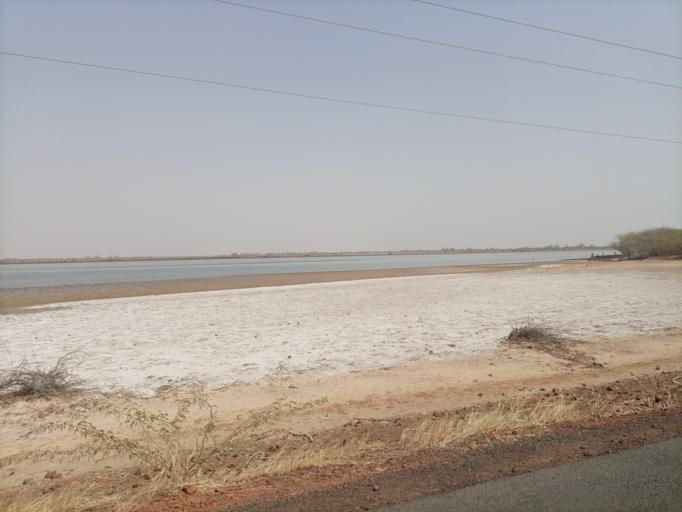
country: SN
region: Fatick
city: Foundiougne
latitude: 14.1892
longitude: -16.4533
